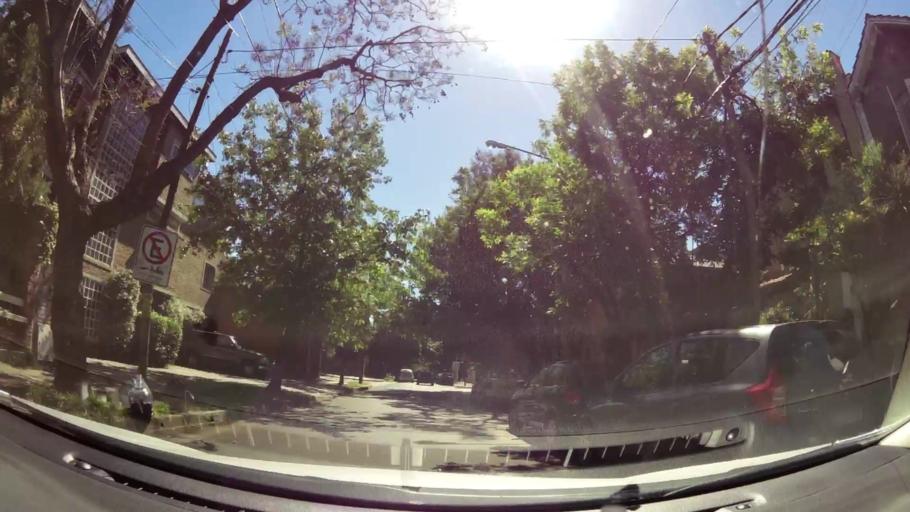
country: AR
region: Buenos Aires
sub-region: Partido de Vicente Lopez
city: Olivos
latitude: -34.5287
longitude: -58.4784
